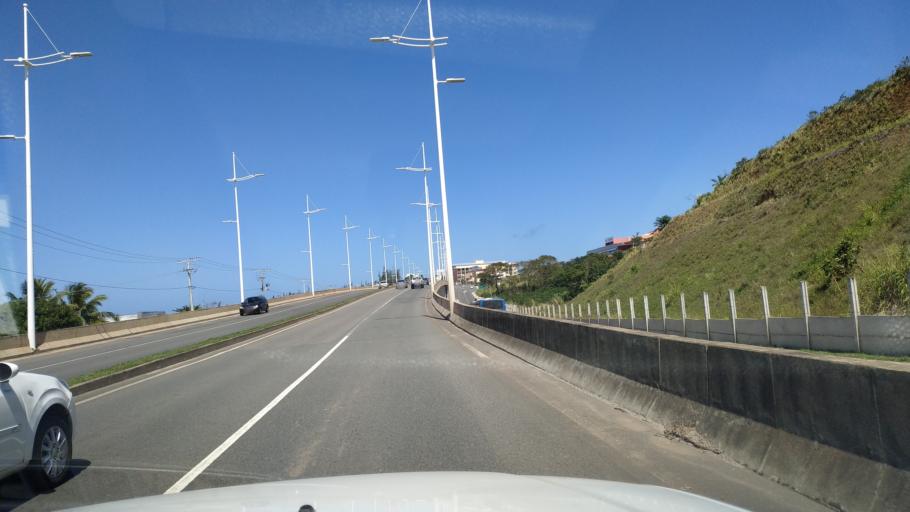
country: BR
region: Bahia
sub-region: Lauro De Freitas
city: Lauro de Freitas
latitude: -12.9355
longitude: -38.3851
